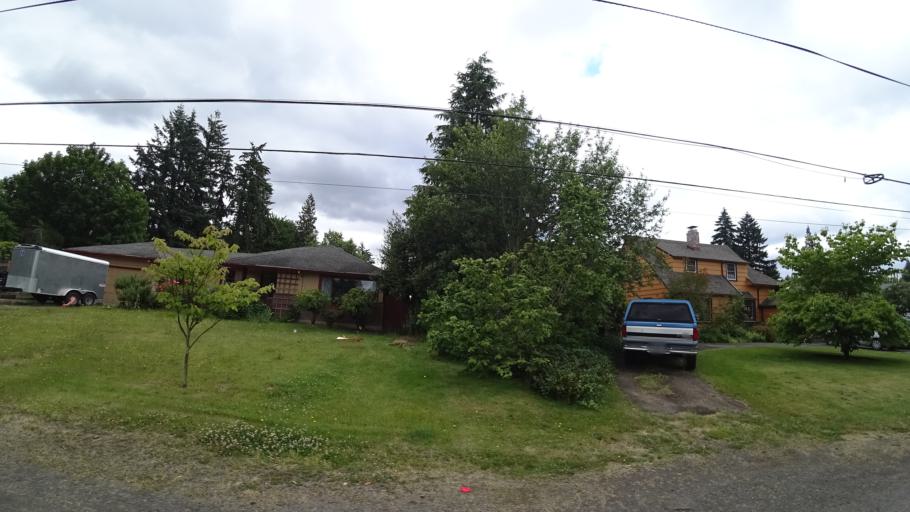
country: US
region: Oregon
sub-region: Multnomah County
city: Lents
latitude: 45.5591
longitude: -122.5916
